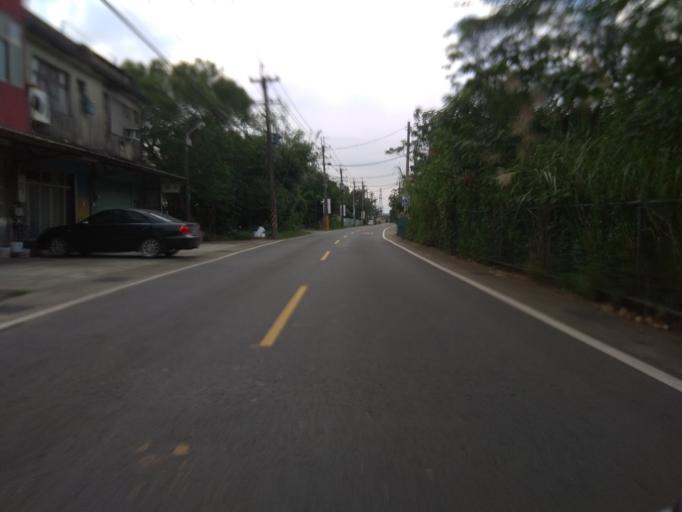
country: TW
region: Taiwan
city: Daxi
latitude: 24.8388
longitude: 121.2074
